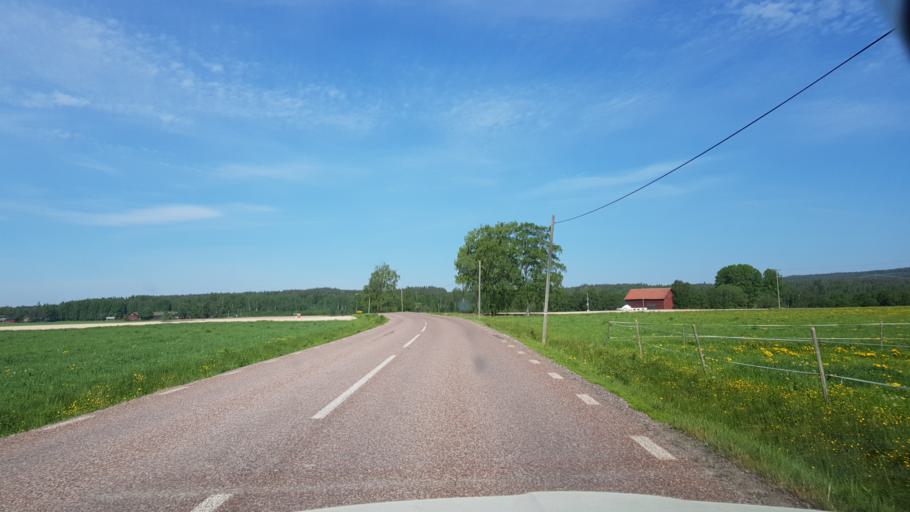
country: SE
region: Dalarna
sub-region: Saters Kommun
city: Saeter
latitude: 60.4157
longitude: 15.7173
